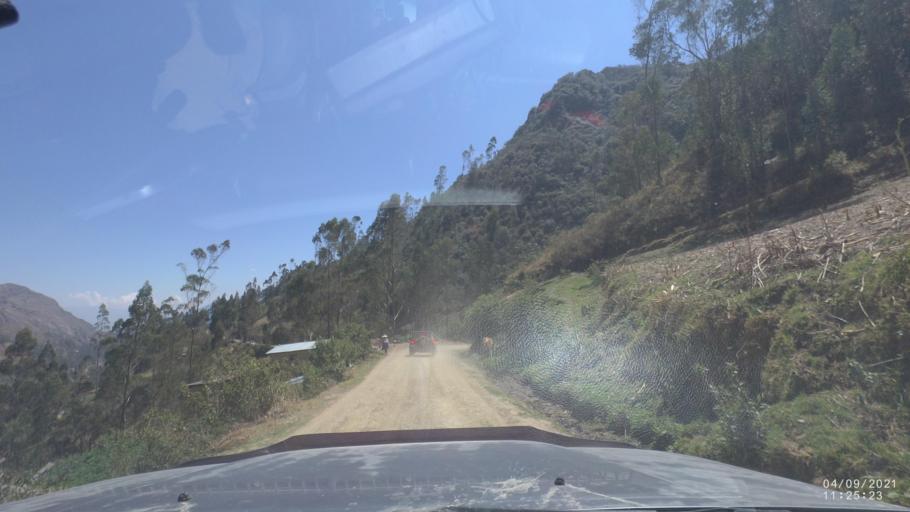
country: BO
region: Cochabamba
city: Colchani
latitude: -17.2563
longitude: -66.5113
